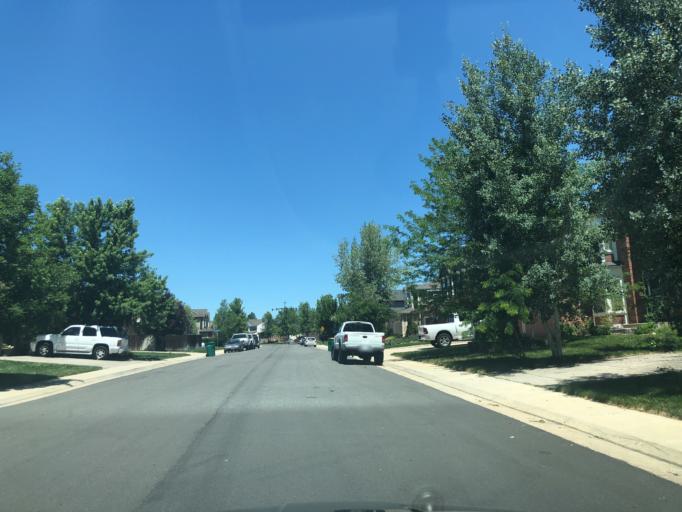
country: US
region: Colorado
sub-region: Arapahoe County
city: Dove Valley
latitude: 39.6101
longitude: -104.7571
